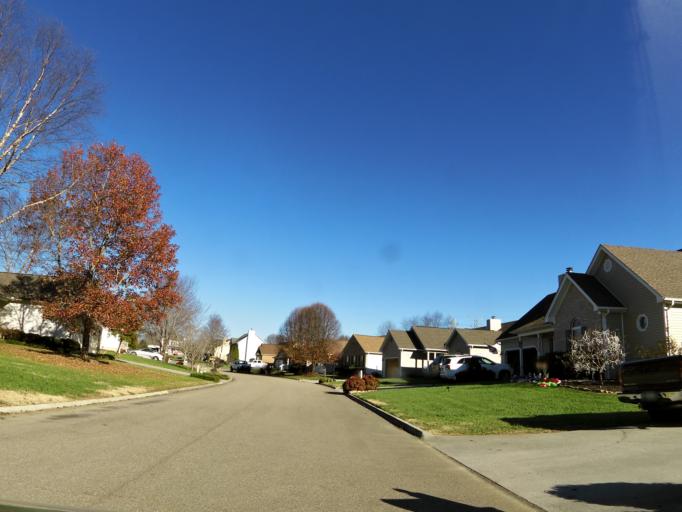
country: US
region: Tennessee
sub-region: Knox County
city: Knoxville
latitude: 36.0323
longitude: -83.9786
